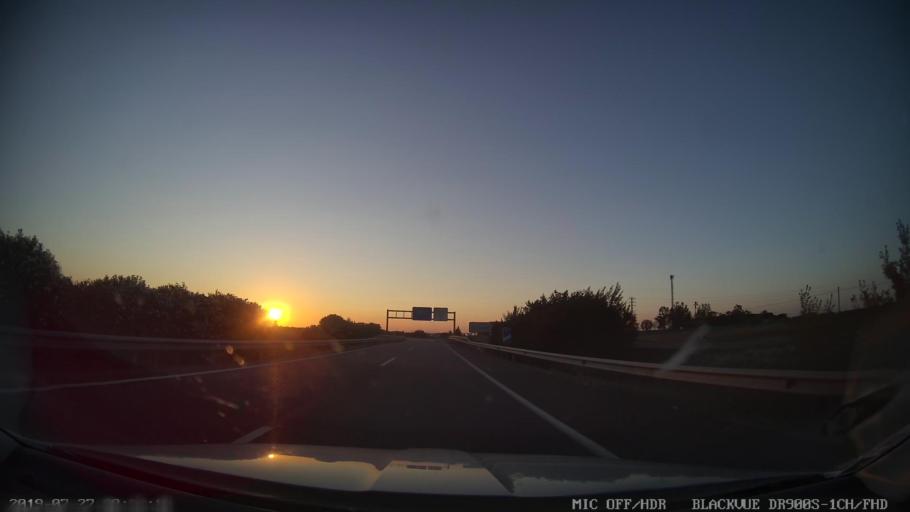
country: ES
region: Extremadura
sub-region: Provincia de Badajoz
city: Talavera La Real
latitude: 38.8621
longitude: -6.7491
